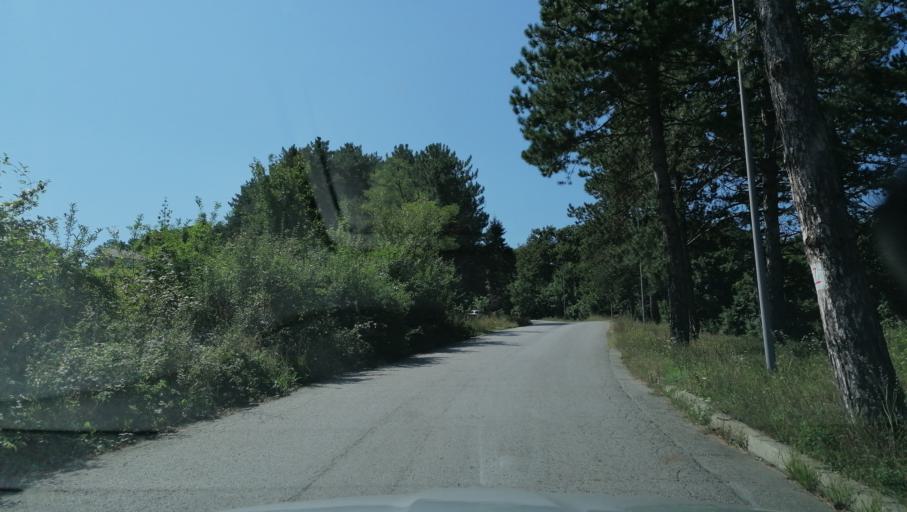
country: RS
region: Central Serbia
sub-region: Kolubarski Okrug
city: Valjevo
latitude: 44.2625
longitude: 19.8800
